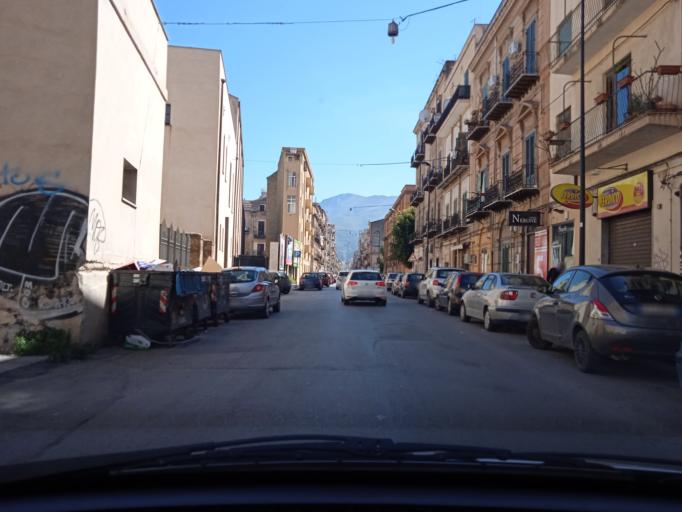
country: IT
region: Sicily
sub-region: Palermo
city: Palermo
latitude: 38.1095
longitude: 13.3643
